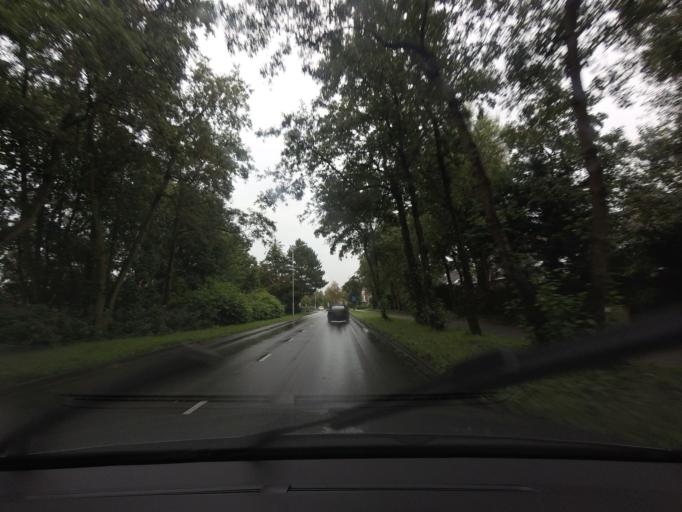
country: NL
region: South Holland
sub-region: Gemeente Voorschoten
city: Voorschoten
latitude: 52.0956
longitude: 4.4098
